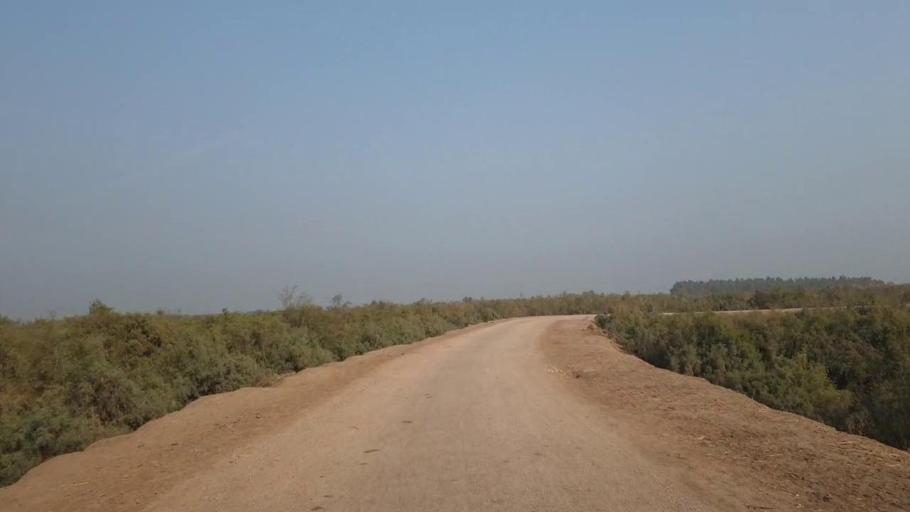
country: PK
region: Sindh
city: Shahdadpur
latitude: 25.9686
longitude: 68.5225
